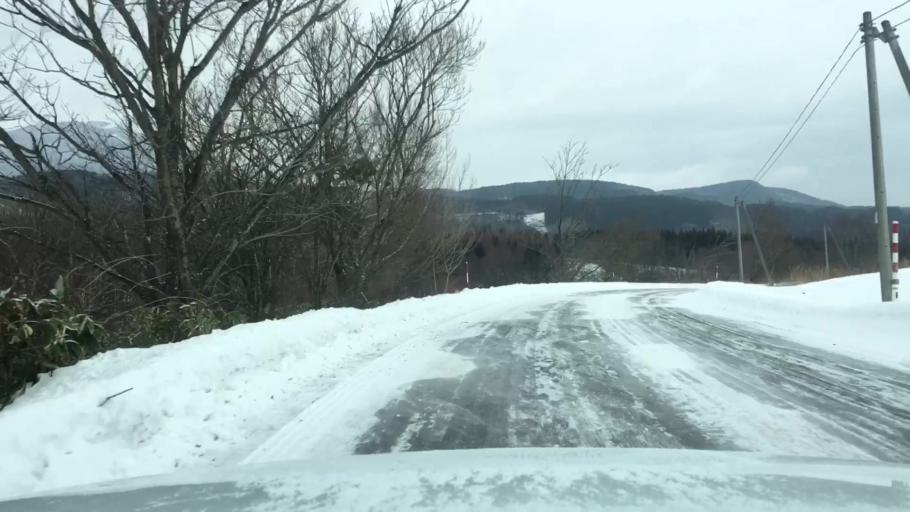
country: JP
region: Iwate
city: Shizukuishi
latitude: 39.9344
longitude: 141.0016
